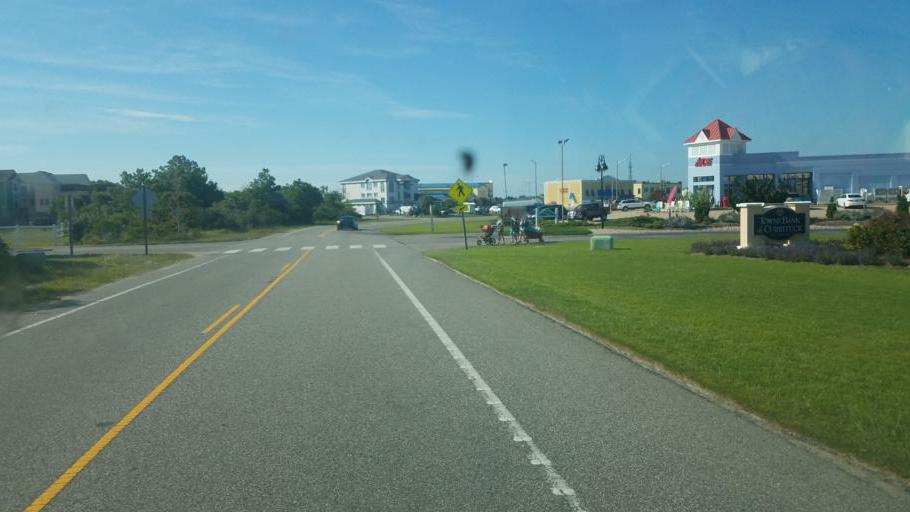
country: US
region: North Carolina
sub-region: Dare County
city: Southern Shores
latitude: 36.3311
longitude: -75.8164
